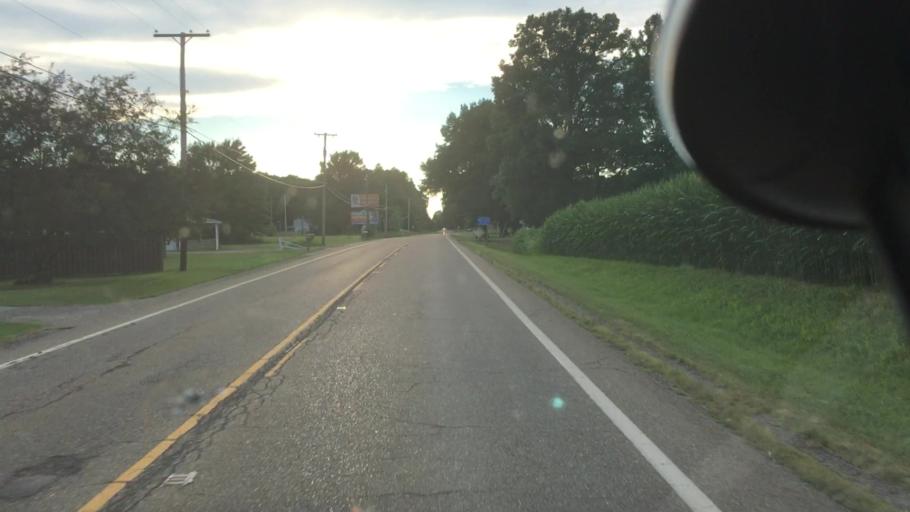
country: US
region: Ohio
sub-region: Columbiana County
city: New Waterford
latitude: 40.8757
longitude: -80.5906
